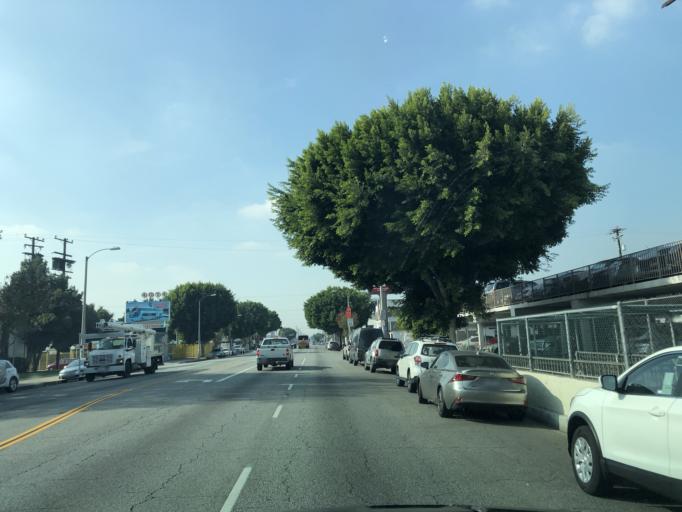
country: US
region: California
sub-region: Los Angeles County
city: East Los Angeles
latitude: 34.0190
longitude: -118.1854
